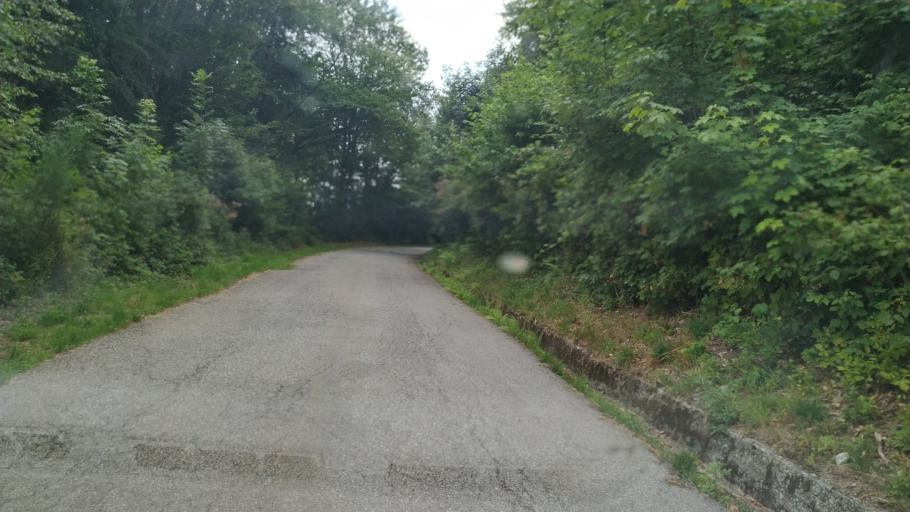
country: IT
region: Piedmont
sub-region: Provincia di Vercelli
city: Varallo
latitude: 45.7993
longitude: 8.2515
